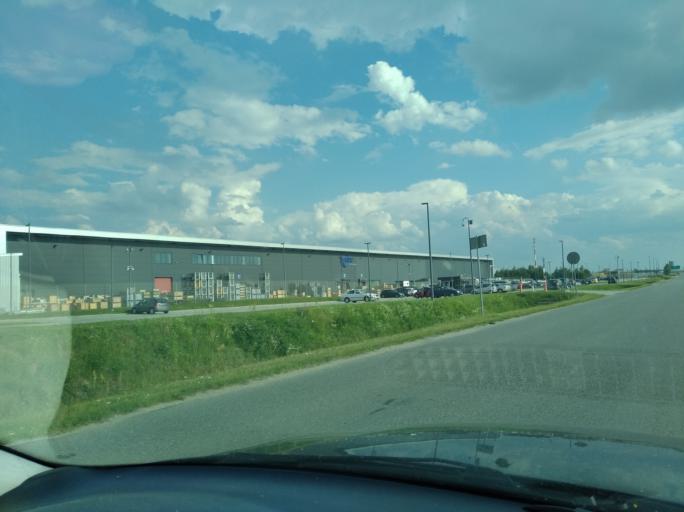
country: PL
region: Subcarpathian Voivodeship
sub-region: Powiat rzeszowski
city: Wysoka Glogowska
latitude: 50.1215
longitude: 22.0234
